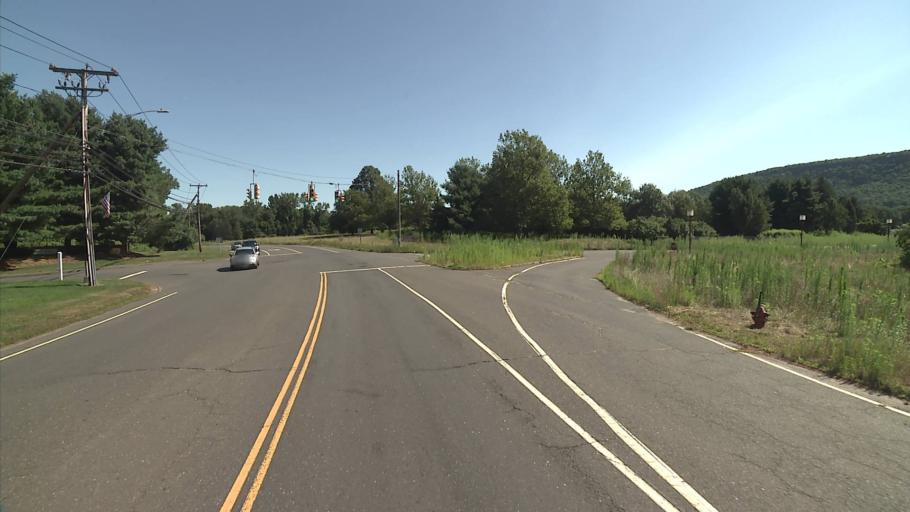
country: US
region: Connecticut
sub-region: Hartford County
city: Weatogue
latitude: 41.8343
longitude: -72.8172
